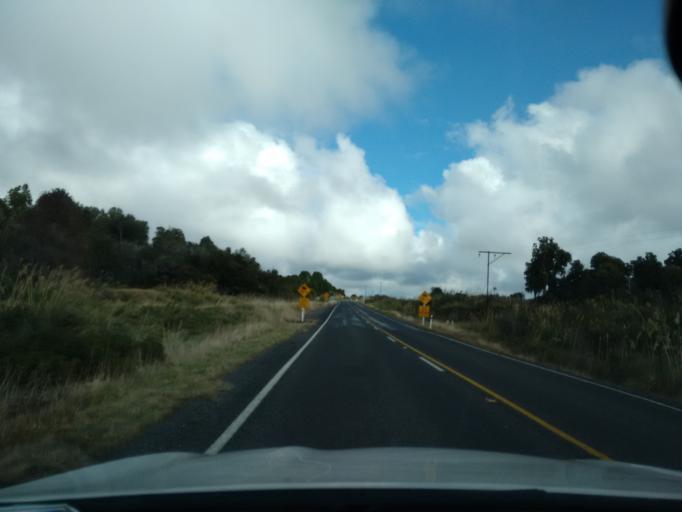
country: NZ
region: Manawatu-Wanganui
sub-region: Ruapehu District
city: Waiouru
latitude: -39.2605
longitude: 175.3892
